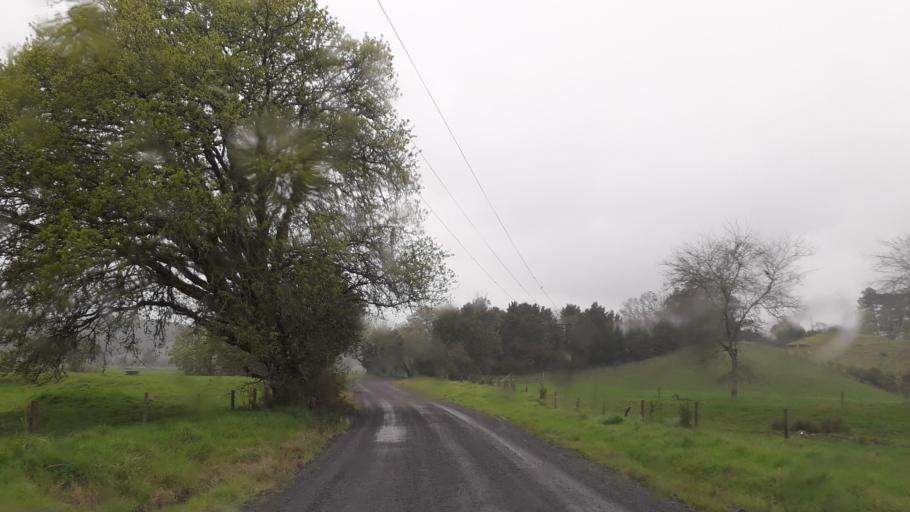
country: NZ
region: Northland
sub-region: Far North District
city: Waimate North
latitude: -35.4781
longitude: 173.6957
